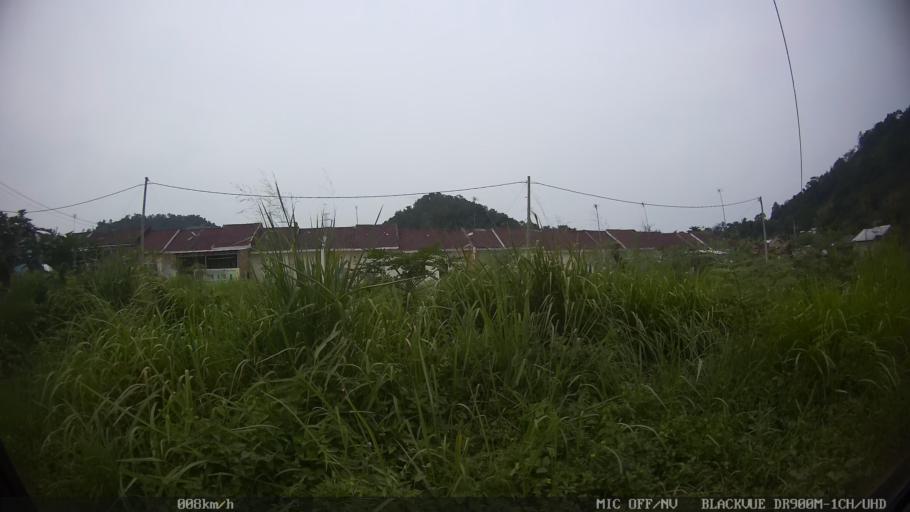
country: ID
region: Lampung
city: Panjang
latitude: -5.4261
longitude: 105.3419
